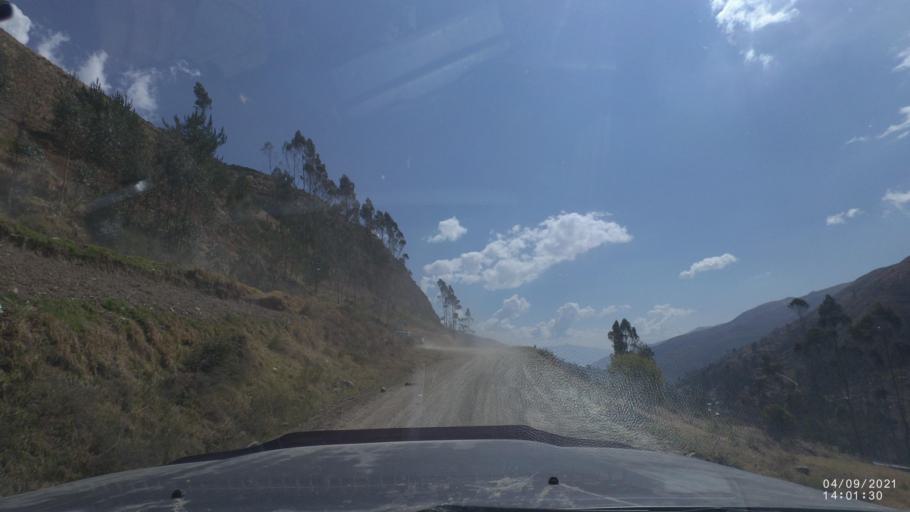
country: BO
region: Cochabamba
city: Sipe Sipe
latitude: -17.2329
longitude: -66.4835
